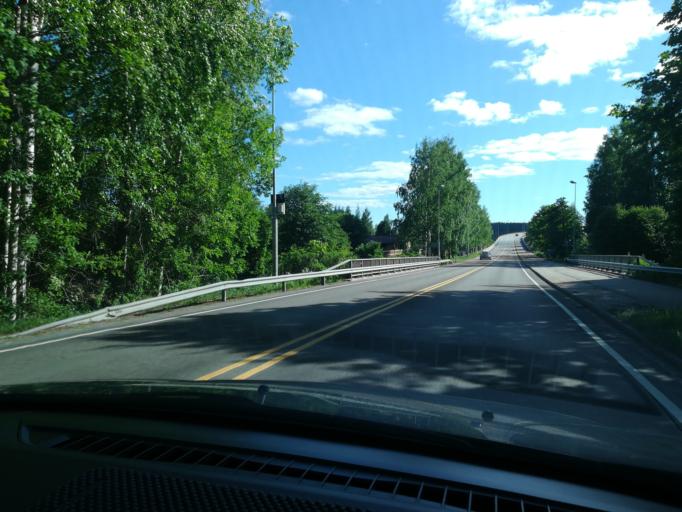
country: FI
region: Southern Savonia
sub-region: Mikkeli
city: Puumala
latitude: 61.5240
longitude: 28.1816
